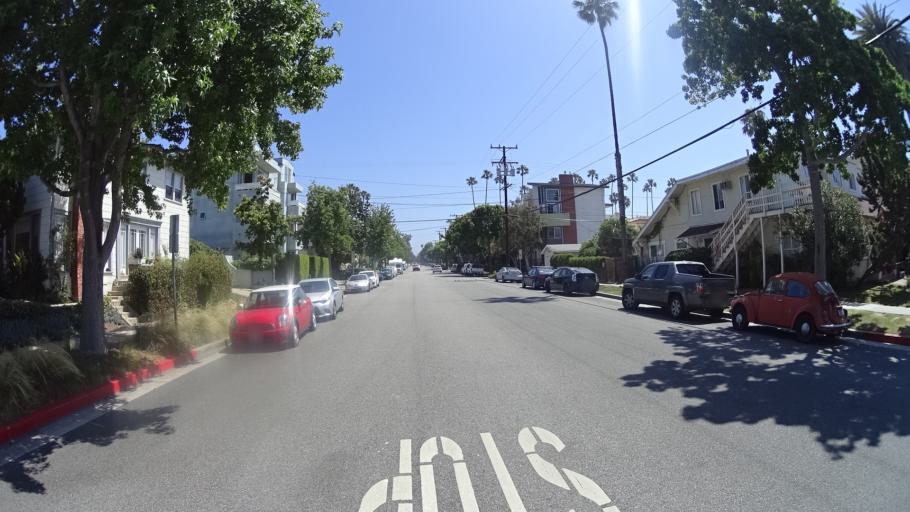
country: US
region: California
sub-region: Los Angeles County
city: Santa Monica
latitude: 34.0233
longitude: -118.5030
